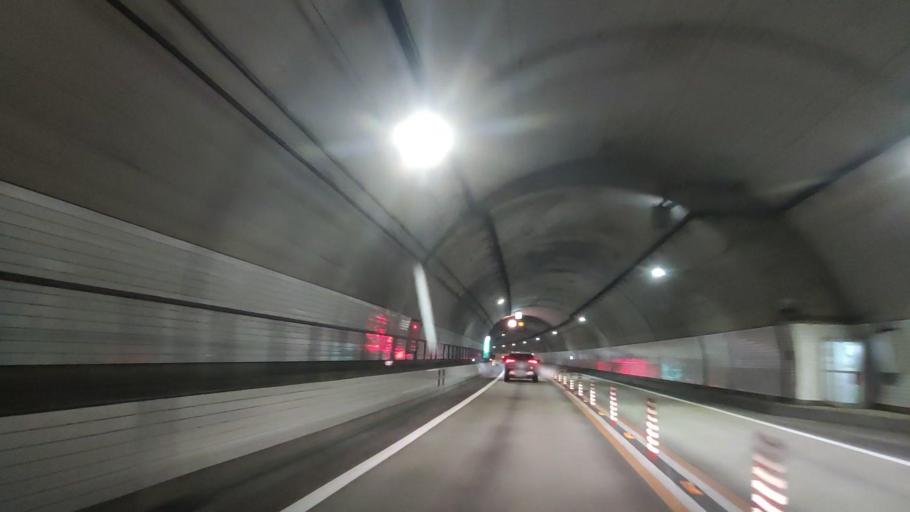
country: JP
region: Kyoto
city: Miyazu
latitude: 35.5613
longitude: 135.1222
